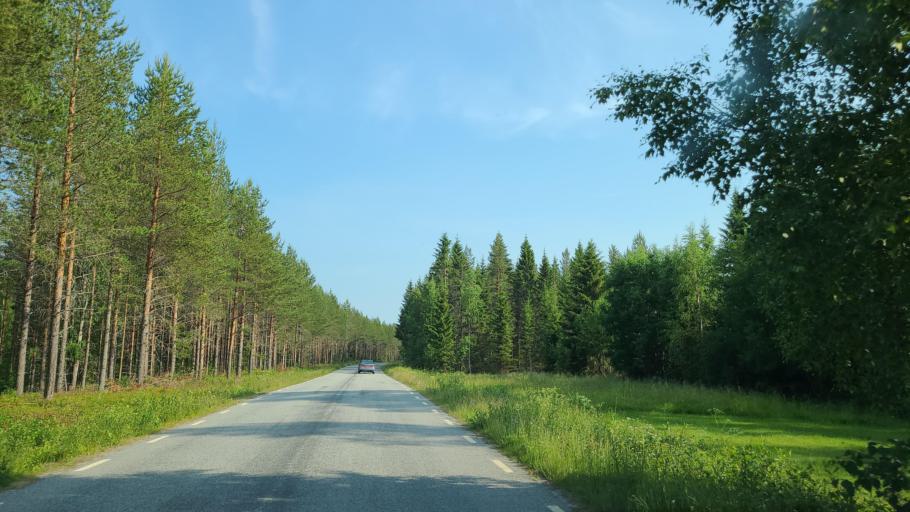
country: SE
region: Vaesterbotten
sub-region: Skelleftea Kommun
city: Burea
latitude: 64.3624
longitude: 21.3322
